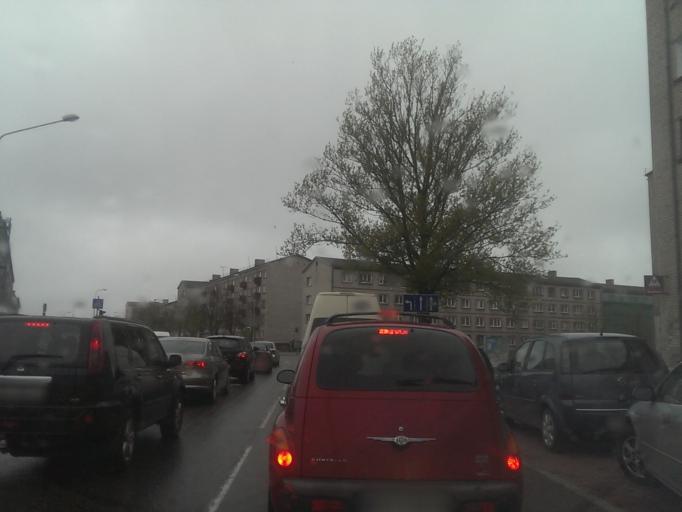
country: LV
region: Ventspils
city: Ventspils
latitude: 57.3896
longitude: 21.5752
